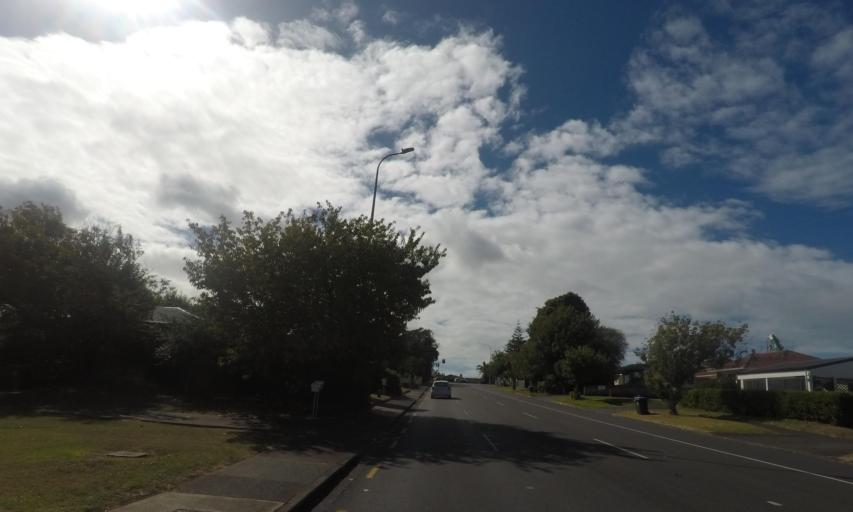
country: NZ
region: Auckland
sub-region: Auckland
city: Tamaki
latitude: -36.9107
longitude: 174.8451
